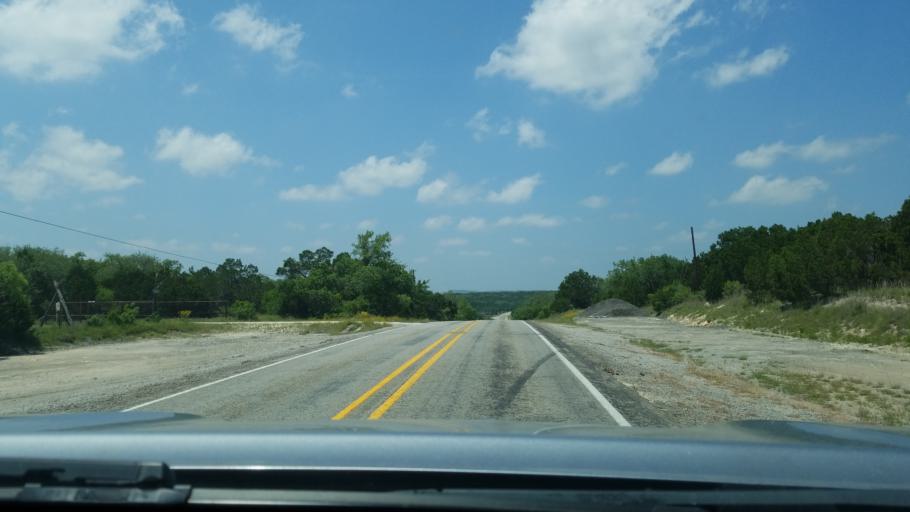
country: US
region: Texas
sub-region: Hays County
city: Woodcreek
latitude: 30.0632
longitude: -98.2129
